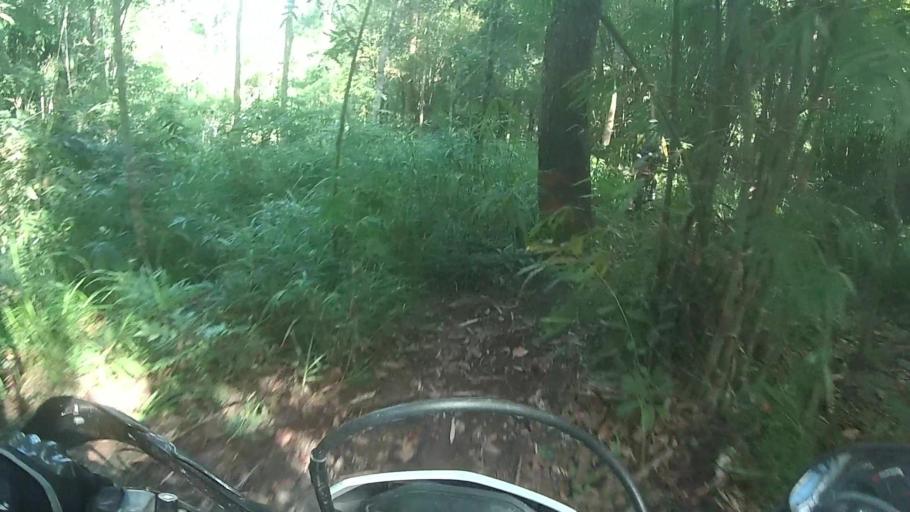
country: TH
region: Chiang Mai
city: Mae Taeng
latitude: 18.9882
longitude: 98.8567
